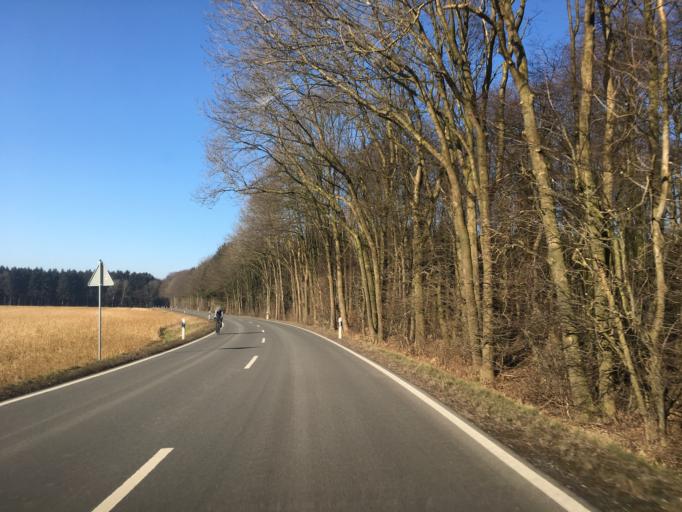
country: DE
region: North Rhine-Westphalia
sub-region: Regierungsbezirk Munster
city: Billerbeck
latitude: 52.0010
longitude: 7.2841
